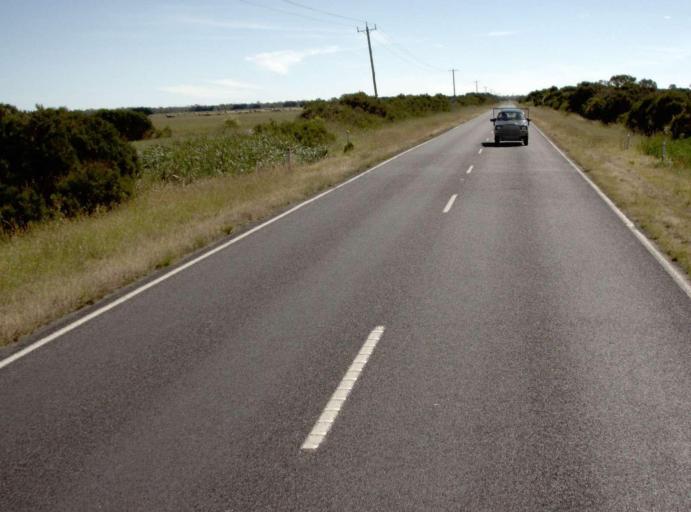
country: AU
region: Victoria
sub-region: Latrobe
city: Traralgon
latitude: -38.6291
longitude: 146.5977
